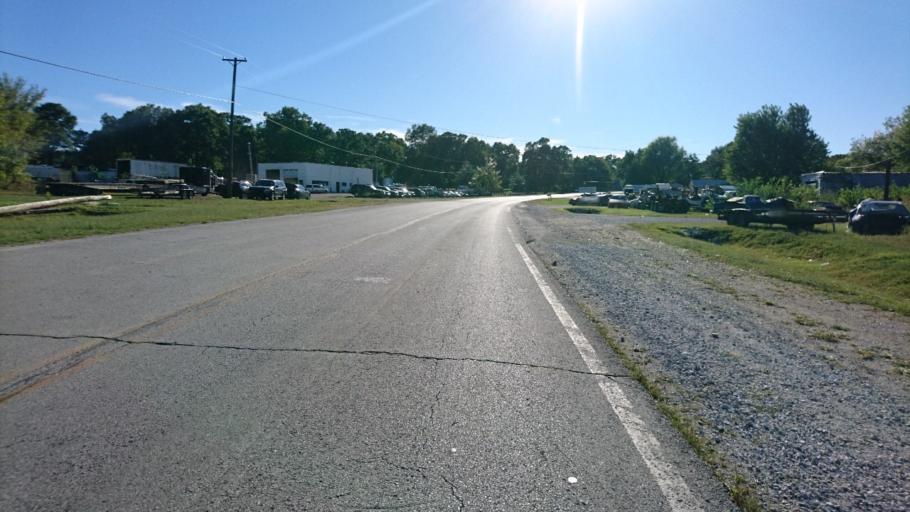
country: US
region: Missouri
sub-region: Jasper County
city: Carthage
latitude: 37.1741
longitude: -94.3477
